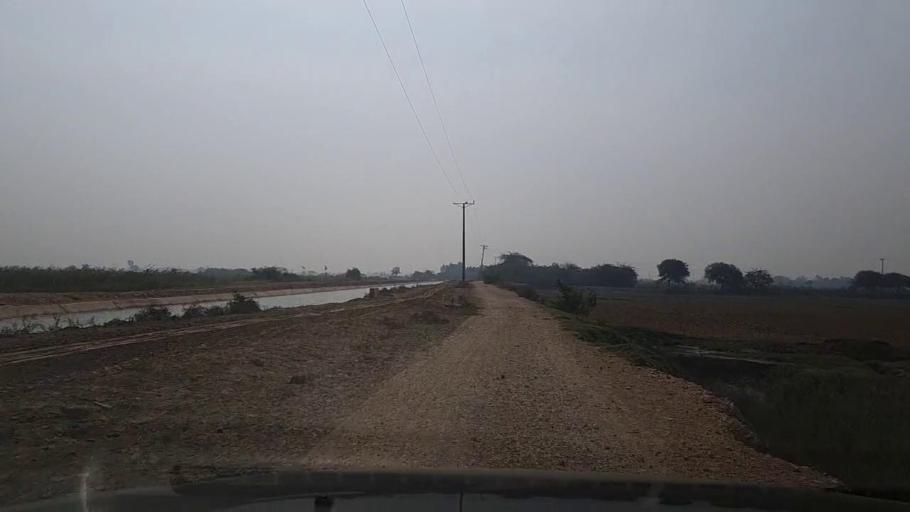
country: PK
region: Sindh
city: Mirpur Sakro
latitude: 24.5279
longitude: 67.8110
